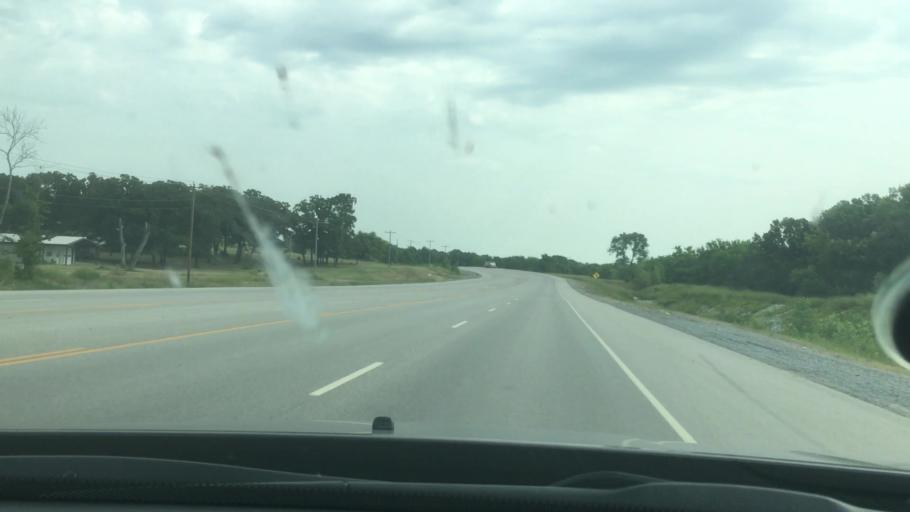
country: US
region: Oklahoma
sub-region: Bryan County
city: Durant
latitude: 34.0461
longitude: -96.3744
